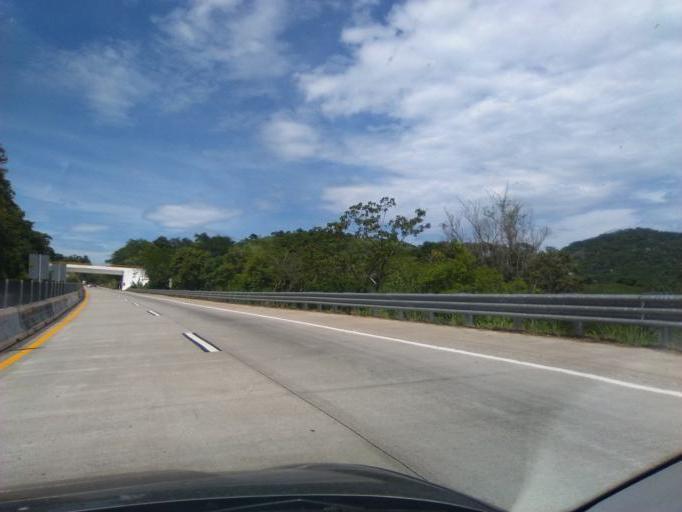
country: MX
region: Guerrero
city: Tierra Colorada
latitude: 17.1431
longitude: -99.5525
